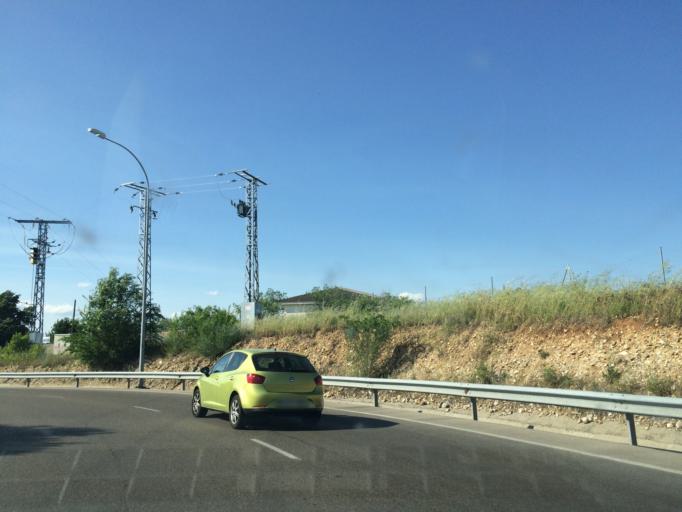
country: ES
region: Madrid
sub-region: Provincia de Madrid
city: Fuente el Saz
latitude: 40.6508
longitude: -3.5104
